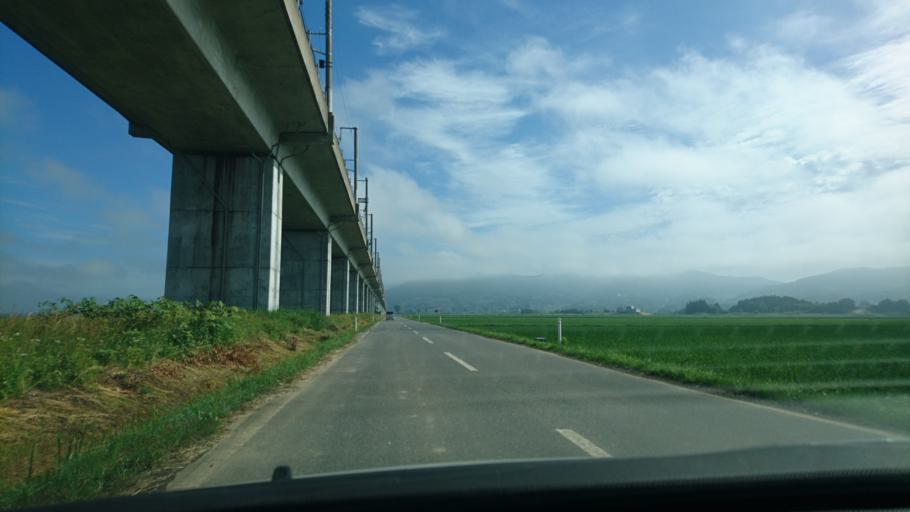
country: JP
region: Iwate
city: Ichinoseki
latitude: 38.9501
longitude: 141.1484
